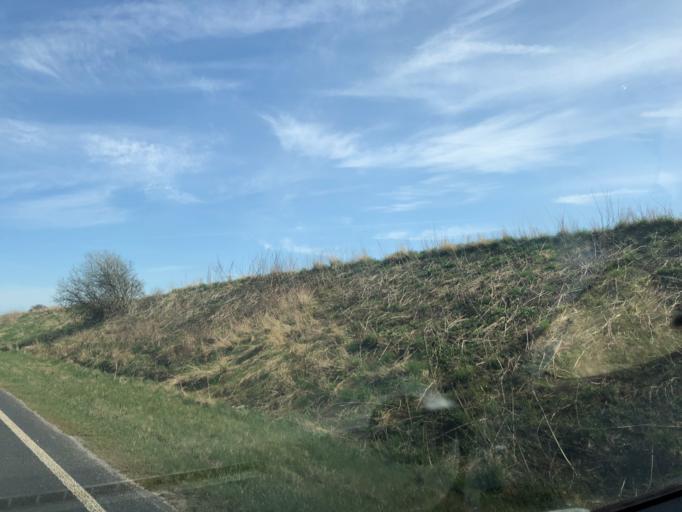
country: DK
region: Zealand
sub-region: Stevns Kommune
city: Harlev
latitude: 55.2783
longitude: 12.2353
